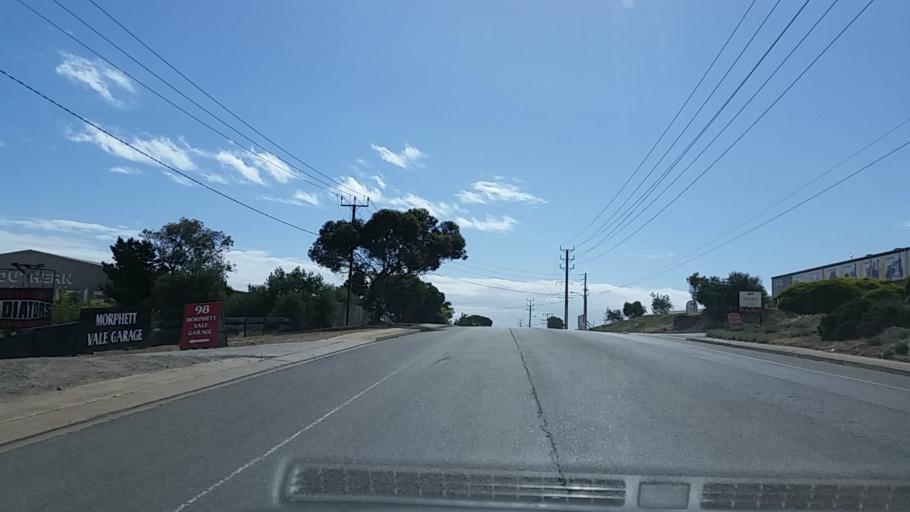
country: AU
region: South Australia
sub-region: Onkaparinga
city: Morphett Vale
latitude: -35.1166
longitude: 138.5043
